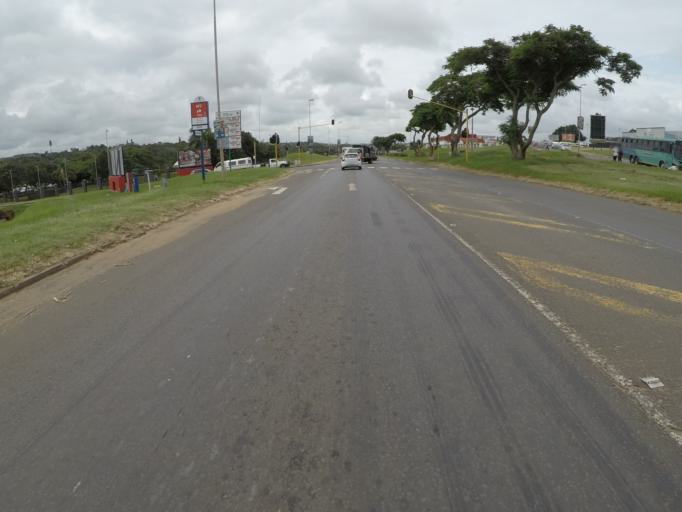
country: ZA
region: KwaZulu-Natal
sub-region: uThungulu District Municipality
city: Empangeni
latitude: -28.7748
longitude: 31.9009
